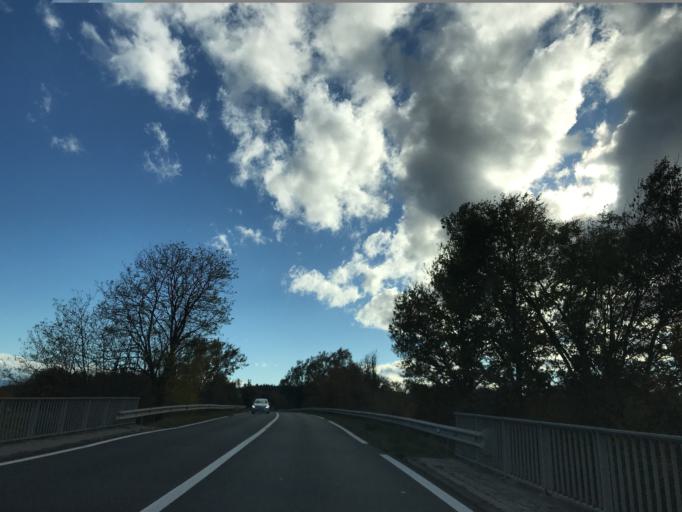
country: FR
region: Auvergne
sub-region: Departement du Puy-de-Dome
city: Peschadoires
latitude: 45.8279
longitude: 3.5023
